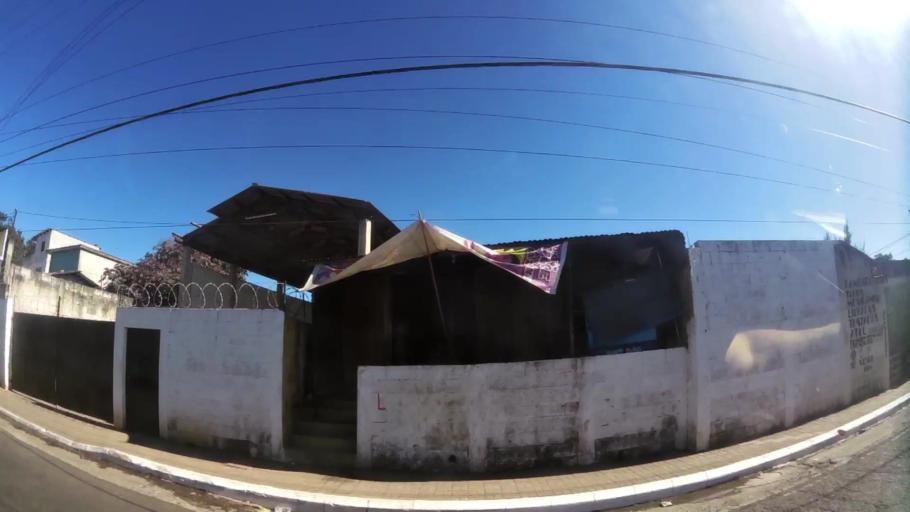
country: GT
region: Guatemala
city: Fraijanes
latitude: 14.4772
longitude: -90.4536
